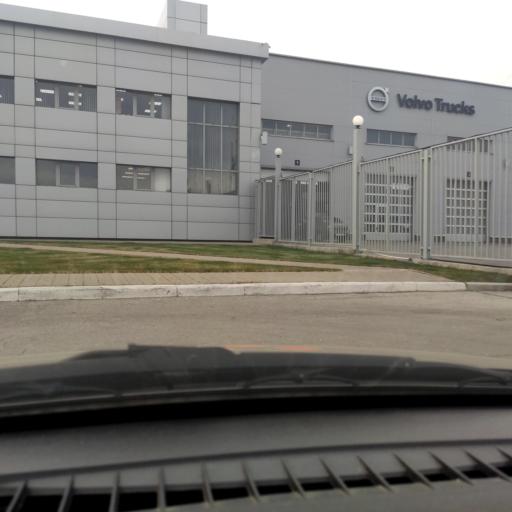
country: RU
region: Samara
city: Tol'yatti
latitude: 53.5562
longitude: 49.3406
